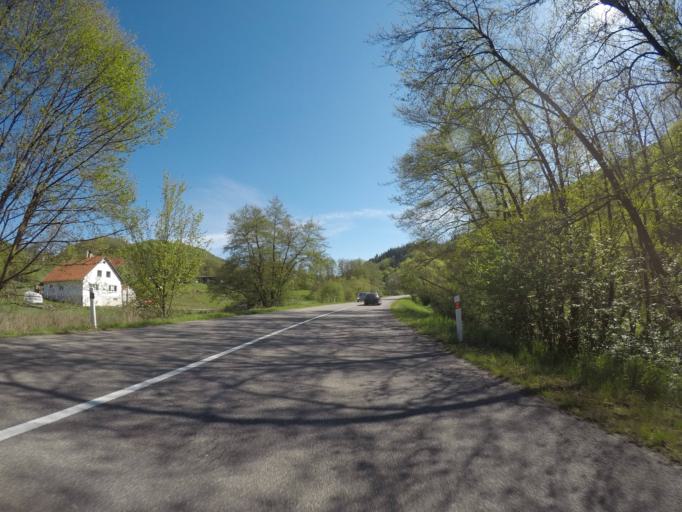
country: SK
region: Banskobystricky
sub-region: Okres Banska Bystrica
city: Banska Stiavnica
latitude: 48.4964
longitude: 18.9549
